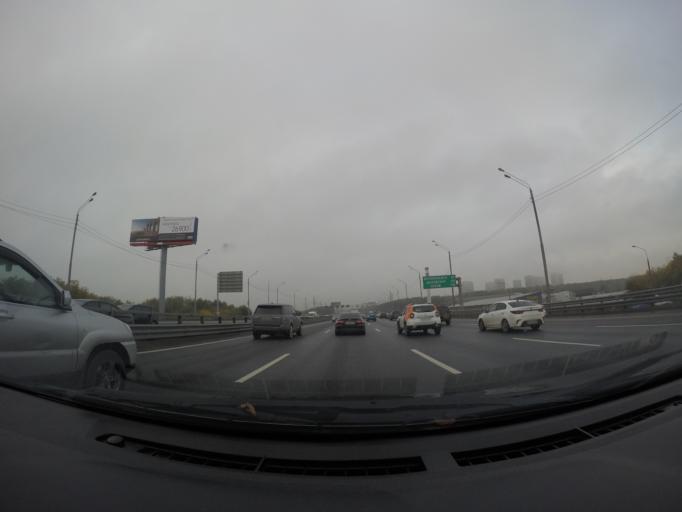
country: RU
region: Moscow
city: Rublevo
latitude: 55.7940
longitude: 37.3555
